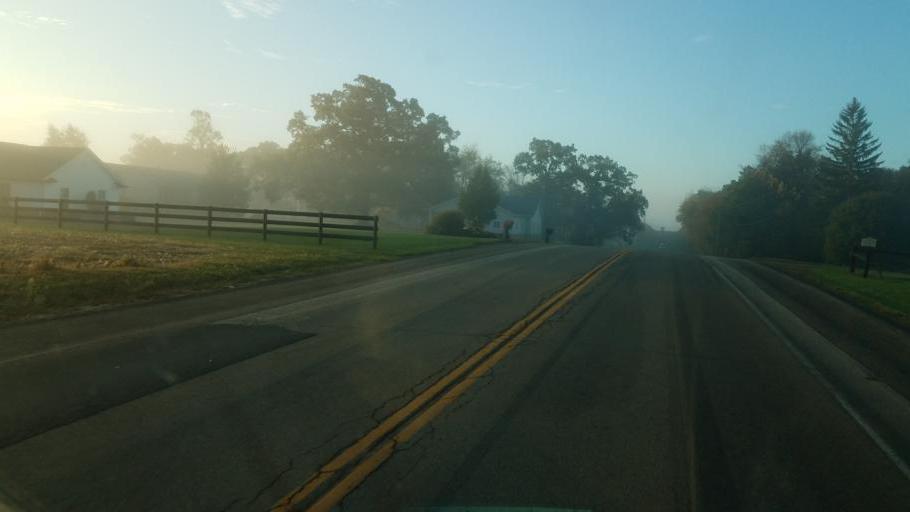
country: US
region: Ohio
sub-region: Holmes County
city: Millersburg
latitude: 40.5900
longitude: -81.7807
